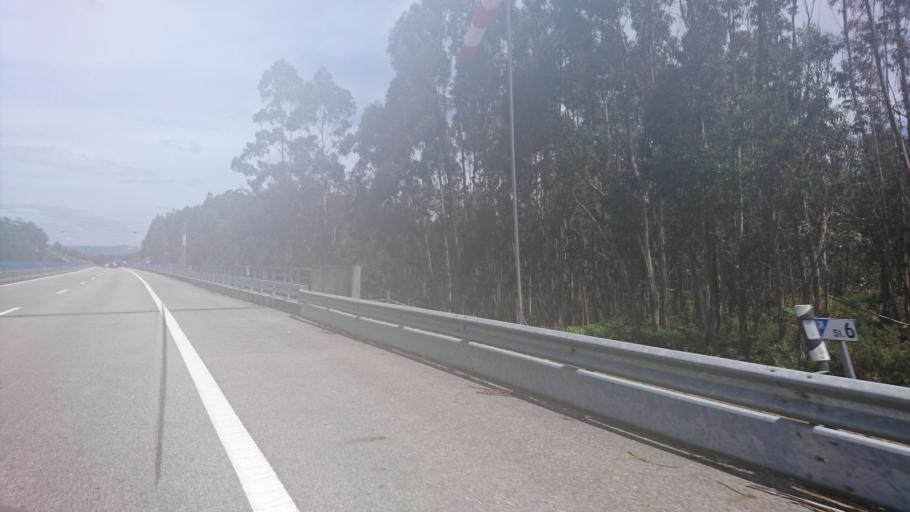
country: PT
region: Porto
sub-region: Vila Nova de Gaia
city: Sandim
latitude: 41.0228
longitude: -8.5103
